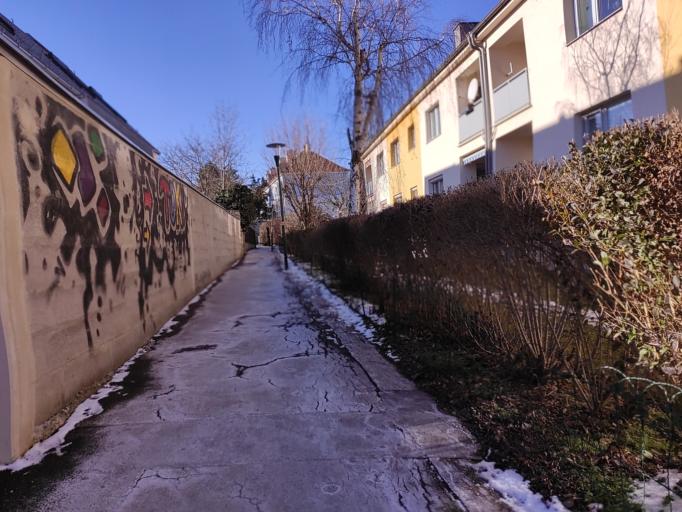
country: AT
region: Lower Austria
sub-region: Politischer Bezirk Modling
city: Brunn am Gebirge
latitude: 48.1091
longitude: 16.2822
